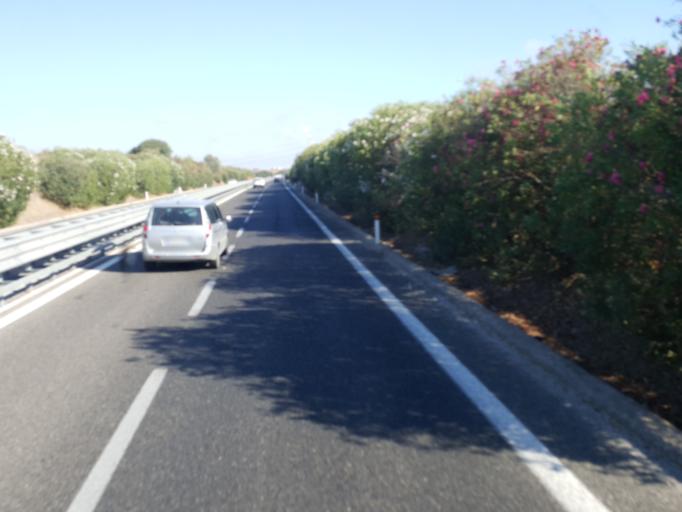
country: IT
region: Latium
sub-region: Provincia di Viterbo
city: Pescia Romana
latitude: 42.3821
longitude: 11.5503
